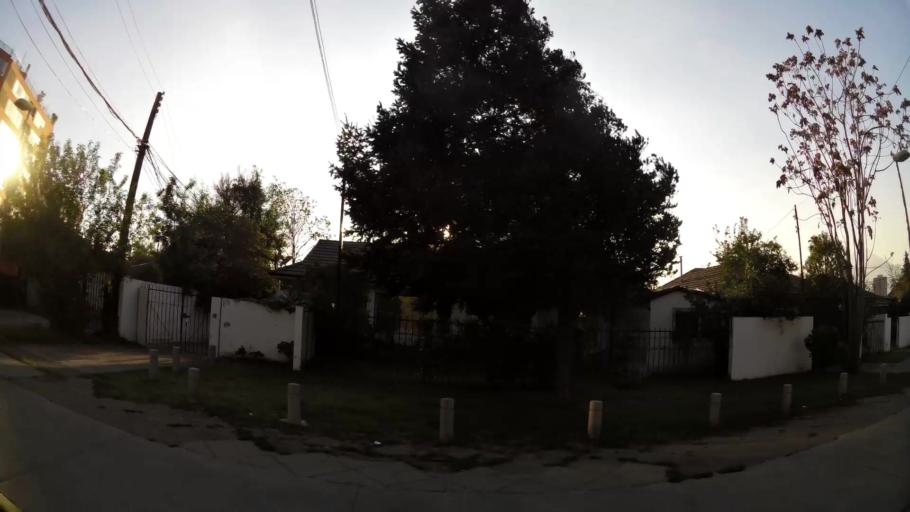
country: CL
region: Santiago Metropolitan
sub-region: Provincia de Santiago
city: Villa Presidente Frei, Nunoa, Santiago, Chile
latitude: -33.3986
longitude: -70.5550
